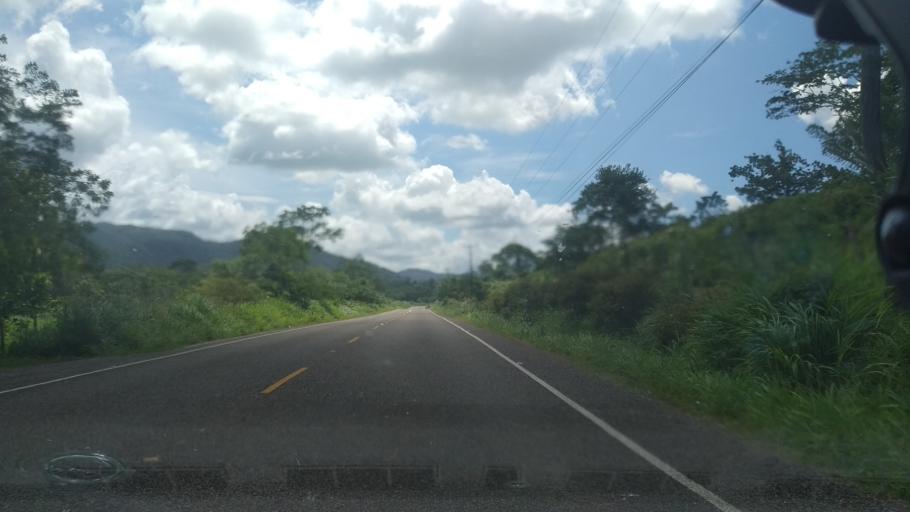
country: BZ
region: Stann Creek
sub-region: Dangriga
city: Dangriga
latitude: 17.0073
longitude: -88.4665
